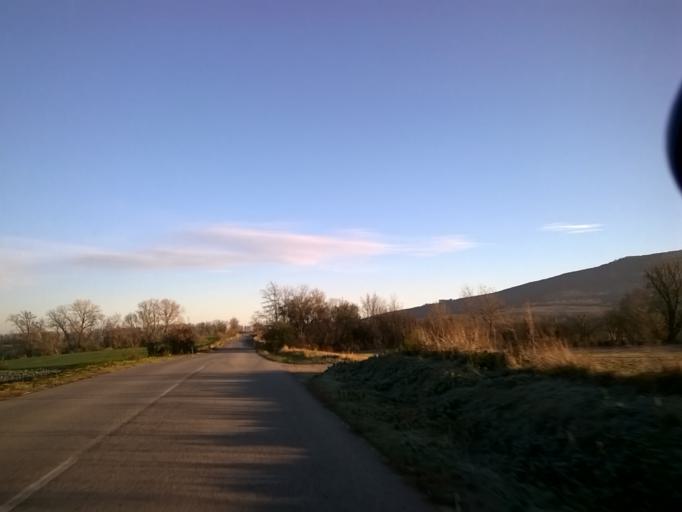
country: SK
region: Nitriansky
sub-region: Okres Nitra
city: Nitra
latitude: 48.4341
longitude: 18.1322
